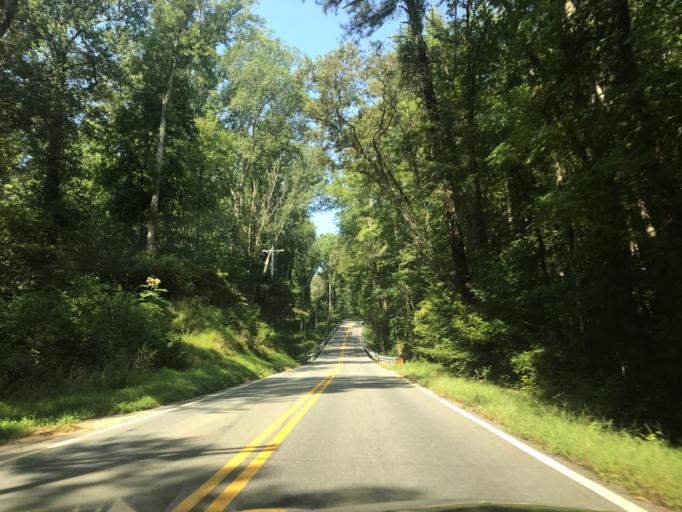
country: US
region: Maryland
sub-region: Calvert County
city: Prince Frederick
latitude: 38.4941
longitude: -76.5944
